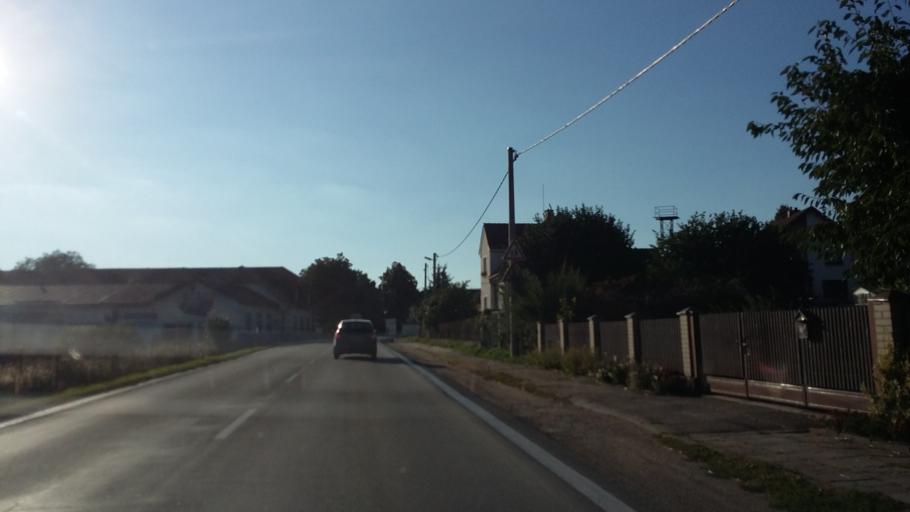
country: CZ
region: Vysocina
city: Merin
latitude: 49.3797
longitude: 15.9292
